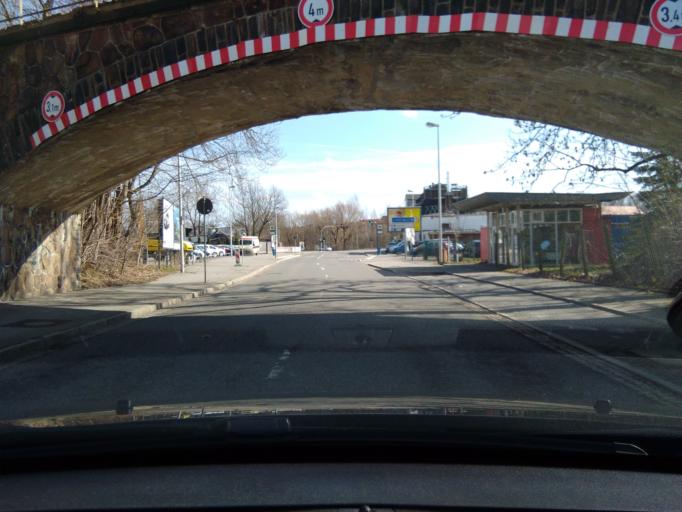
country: DE
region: Saxony
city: Wittgensdorf
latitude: 50.8337
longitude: 12.8702
